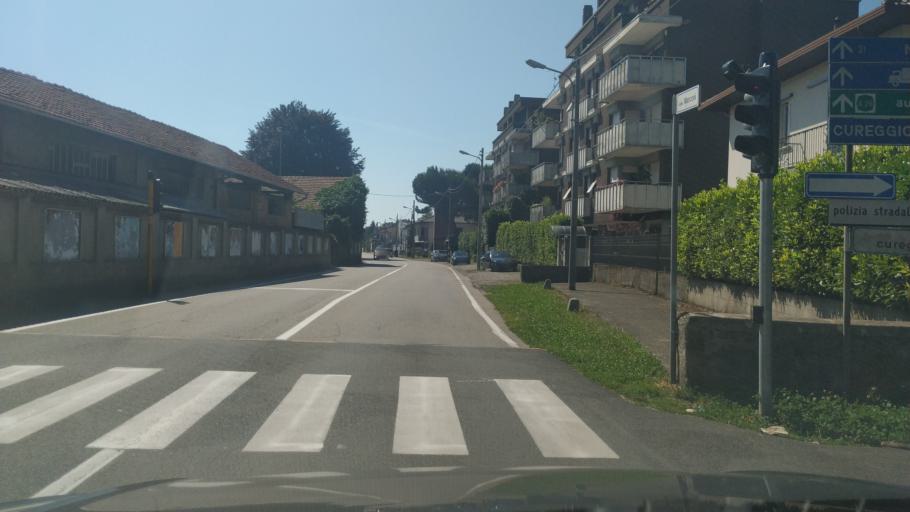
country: IT
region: Piedmont
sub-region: Provincia di Novara
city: Borgomanero
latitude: 45.6943
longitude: 8.4614
